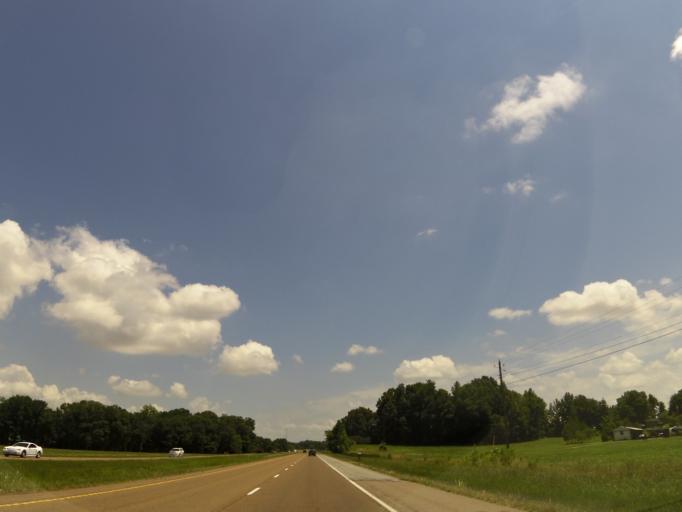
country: US
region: Tennessee
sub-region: Lauderdale County
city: Halls
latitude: 35.9273
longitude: -89.2833
